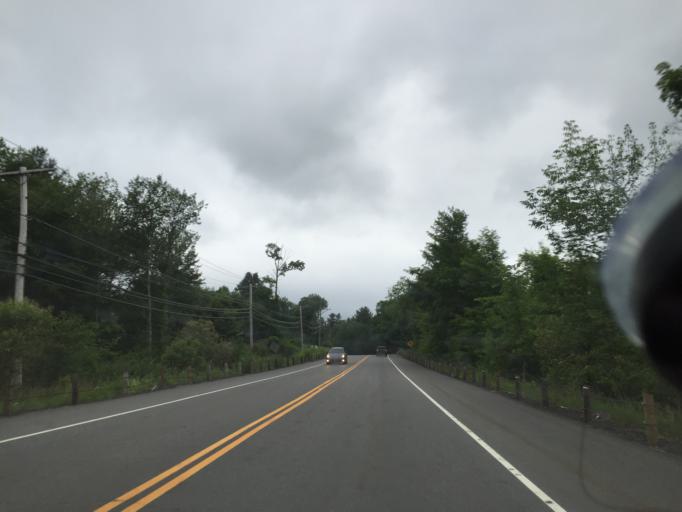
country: US
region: Connecticut
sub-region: Litchfield County
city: Litchfield
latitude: 41.8306
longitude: -73.2431
